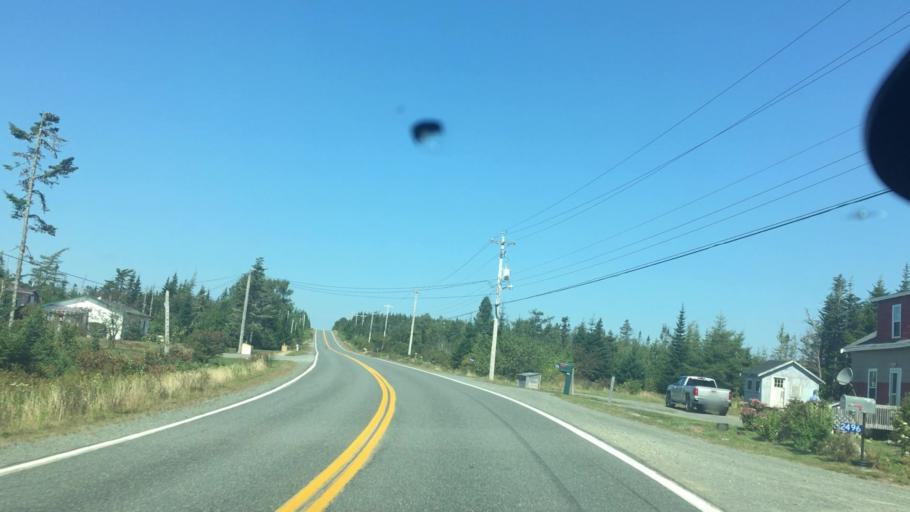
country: CA
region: Nova Scotia
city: Antigonish
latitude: 45.0005
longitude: -62.0997
